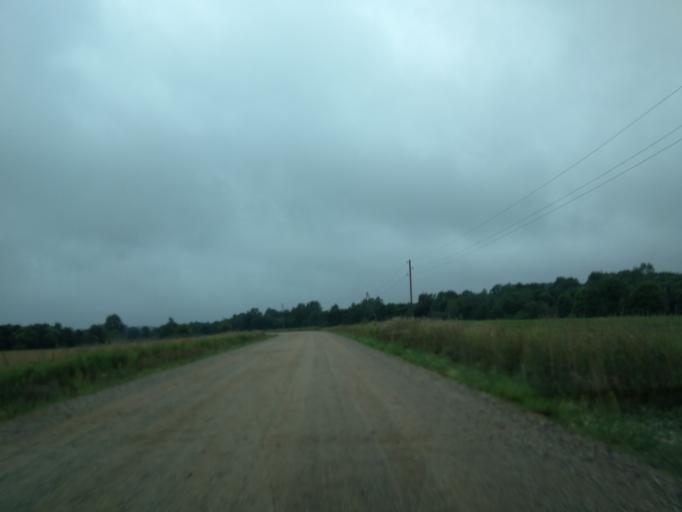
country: LV
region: Vilanu
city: Vilani
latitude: 56.3715
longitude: 27.0241
